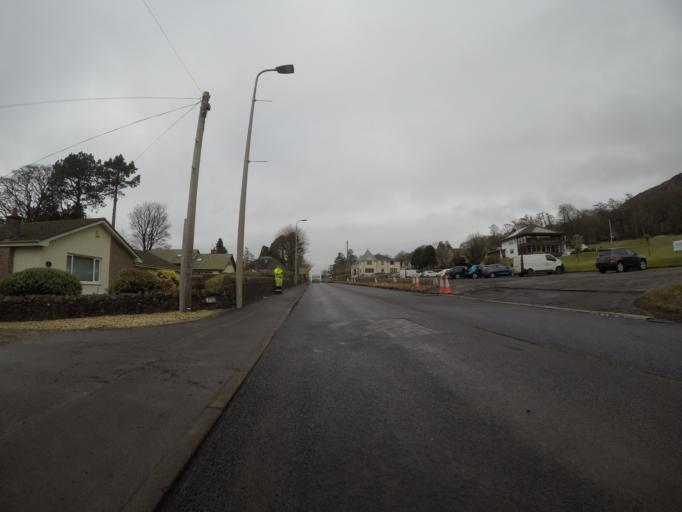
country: GB
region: Scotland
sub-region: North Ayrshire
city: Largs
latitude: 55.7829
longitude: -4.8568
